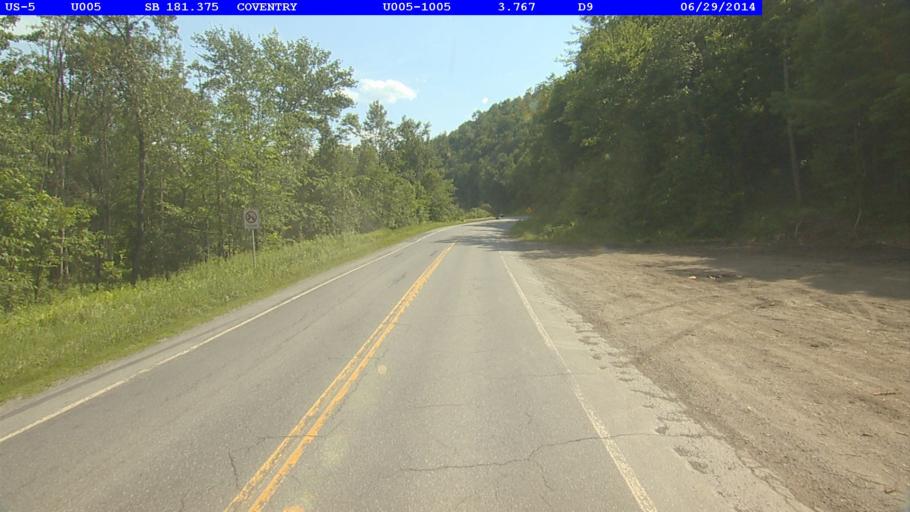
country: US
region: Vermont
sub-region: Orleans County
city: Newport
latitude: 44.9084
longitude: -72.2405
